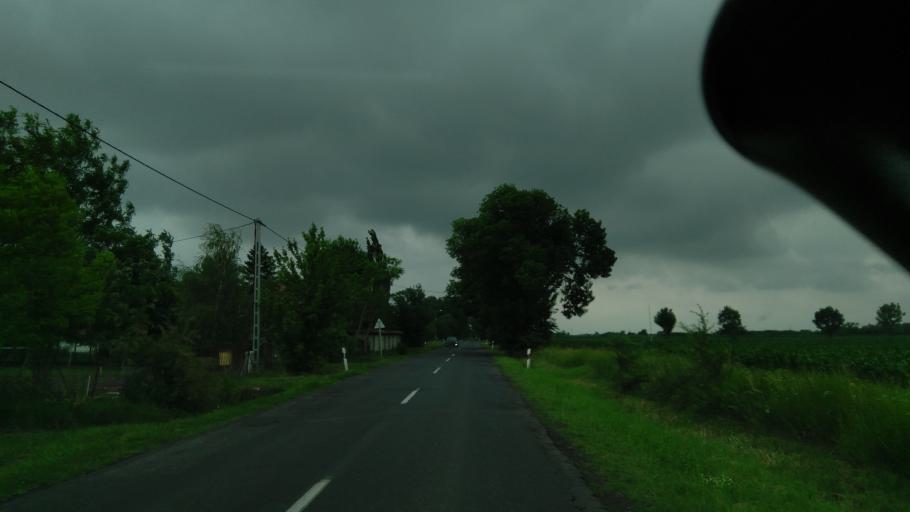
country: HU
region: Bekes
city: Szabadkigyos
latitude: 46.6376
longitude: 21.0983
